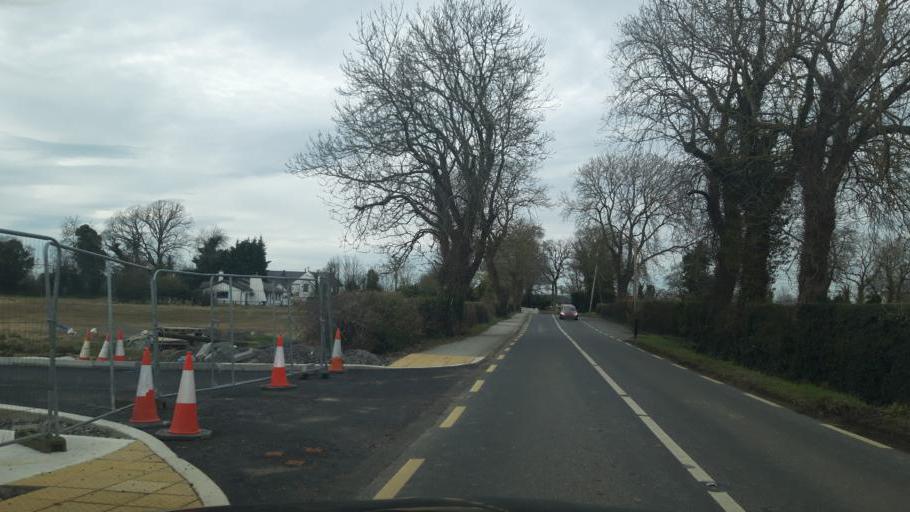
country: IE
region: Leinster
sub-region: Kildare
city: Clane
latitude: 53.3351
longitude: -6.6760
